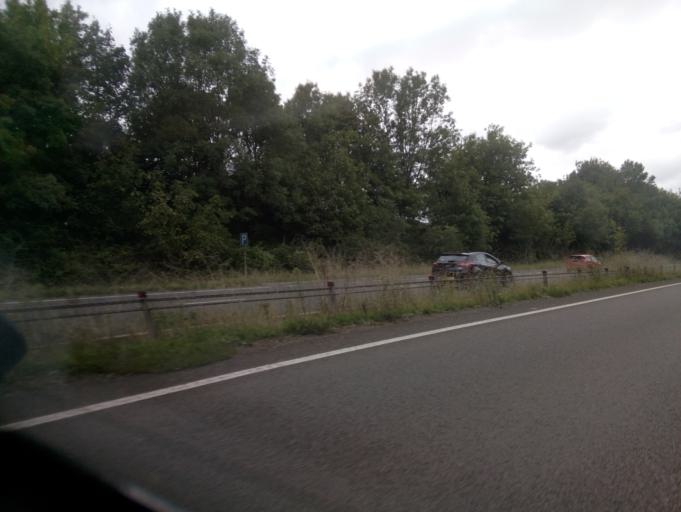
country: GB
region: England
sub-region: Devon
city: Kingskerswell
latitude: 50.4783
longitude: -3.5825
